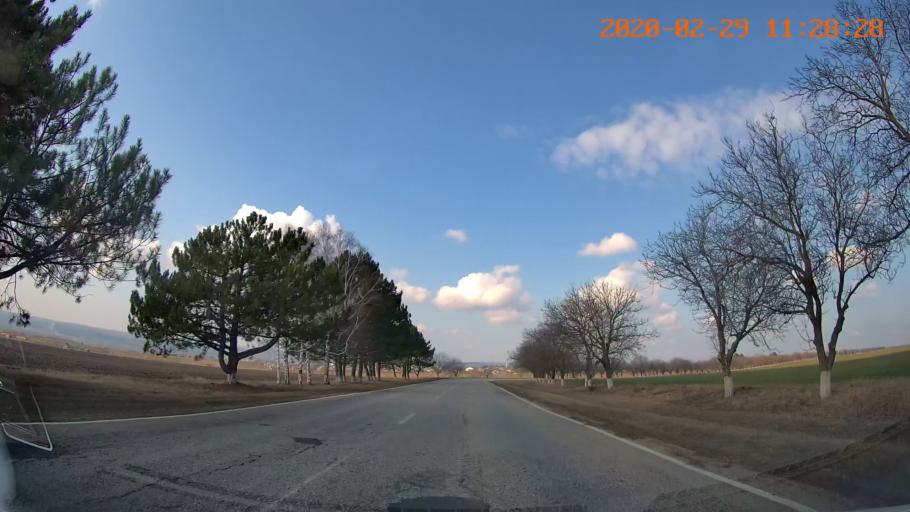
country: MD
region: Telenesti
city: Cocieri
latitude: 47.4814
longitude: 29.1350
